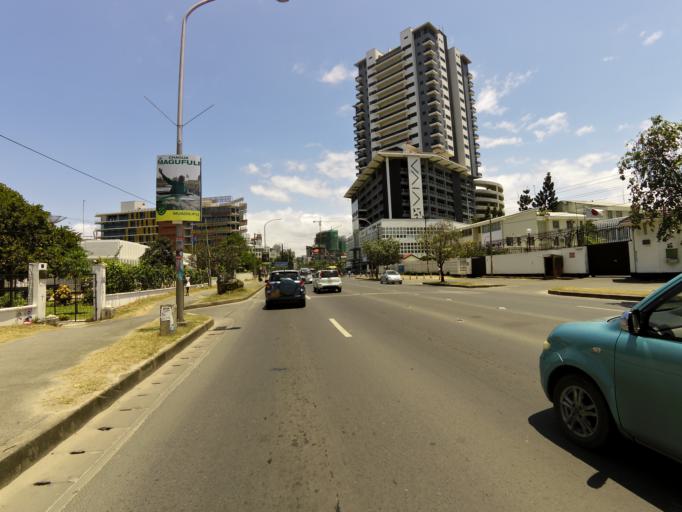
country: TZ
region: Dar es Salaam
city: Dar es Salaam
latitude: -6.8083
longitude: 39.2867
